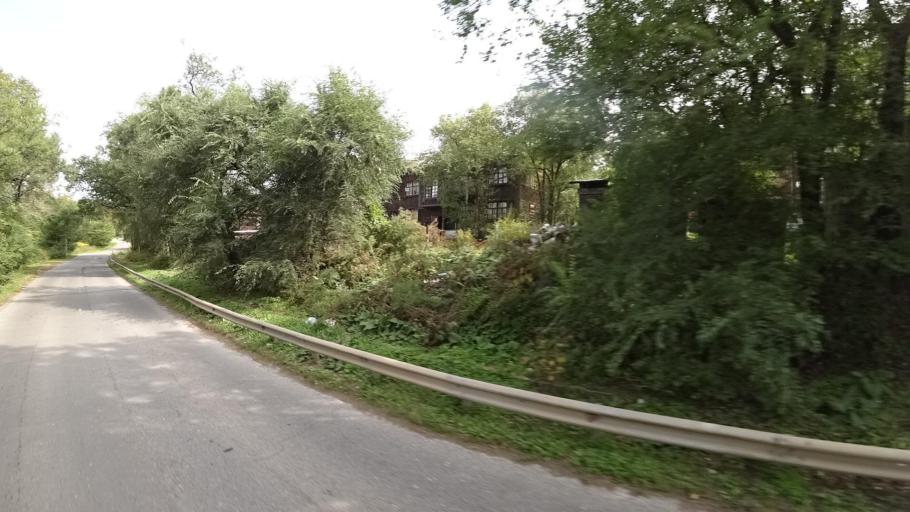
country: RU
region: Jewish Autonomous Oblast
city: Khingansk
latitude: 49.0088
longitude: 131.0604
